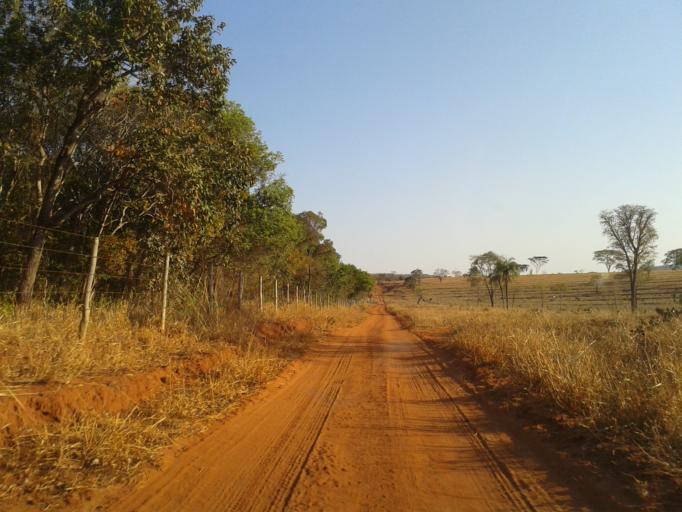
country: BR
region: Minas Gerais
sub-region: Campina Verde
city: Campina Verde
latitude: -19.2513
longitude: -49.6102
